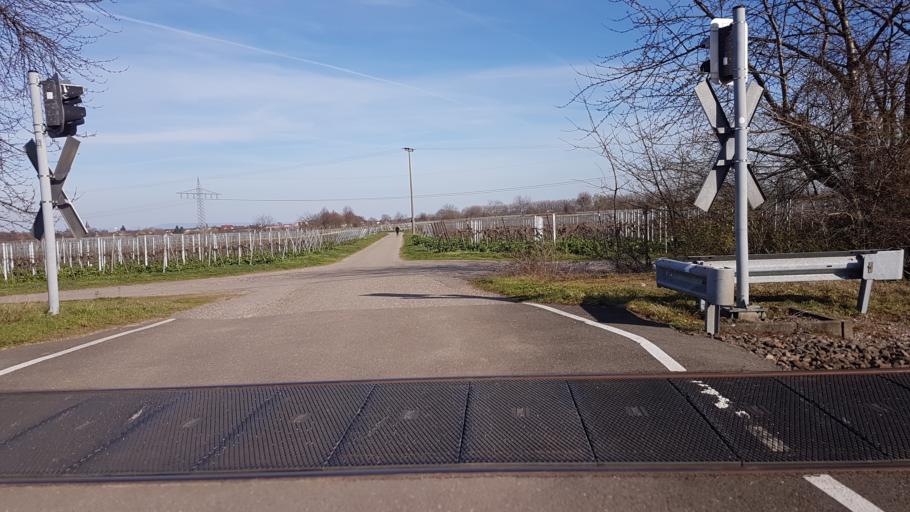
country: DE
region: Rheinland-Pfalz
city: Maikammer
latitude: 49.2957
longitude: 8.1443
